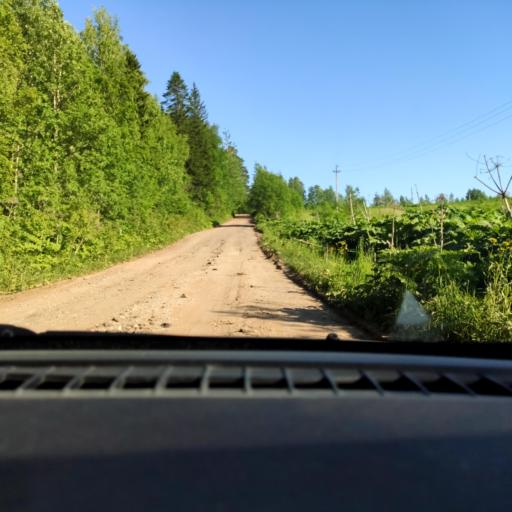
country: RU
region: Perm
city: Overyata
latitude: 58.1265
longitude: 55.8759
